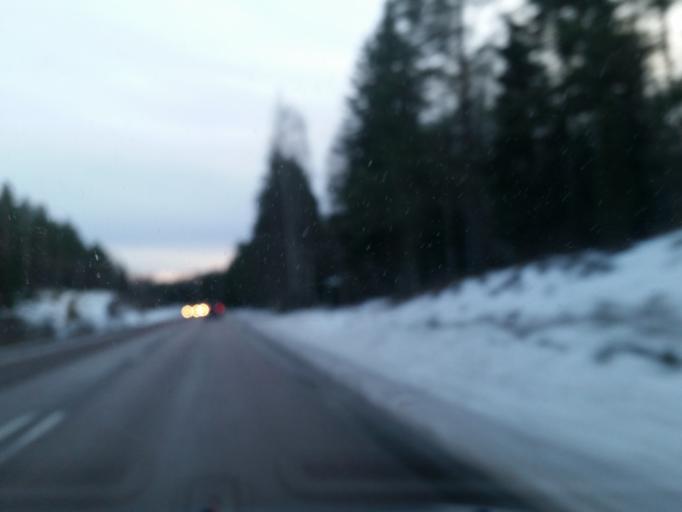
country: SE
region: Gaevleborg
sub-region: Sandvikens Kommun
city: Sandviken
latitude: 60.6446
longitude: 16.7392
